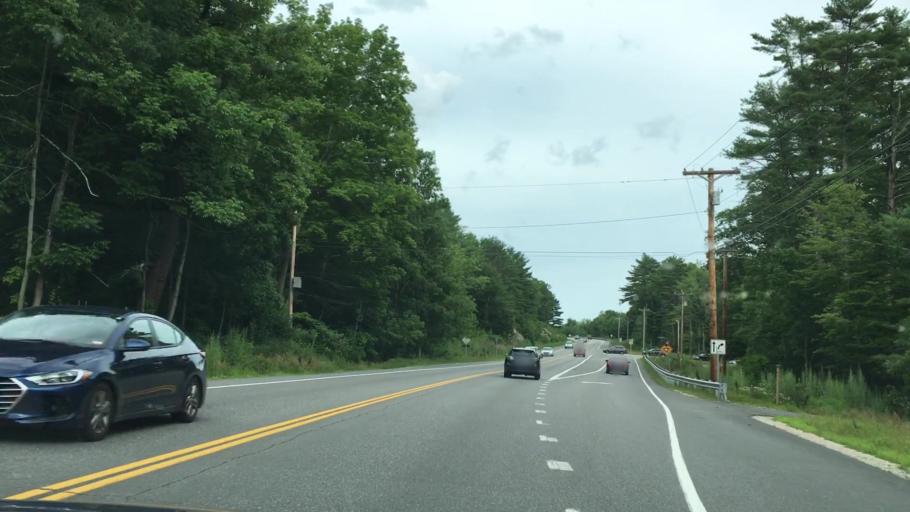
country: US
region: New Hampshire
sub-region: Belknap County
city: Meredith
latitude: 43.6232
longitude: -71.5538
